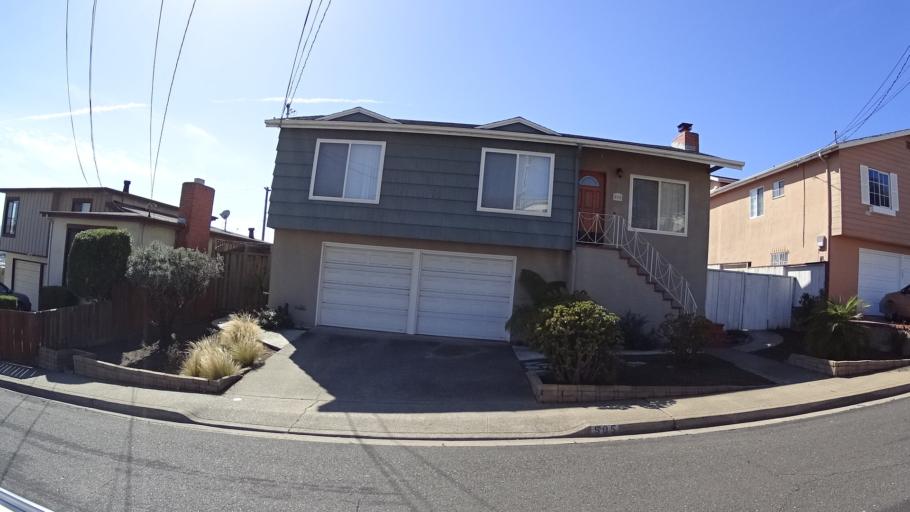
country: US
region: California
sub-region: San Mateo County
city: South San Francisco
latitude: 37.6604
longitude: -122.4148
